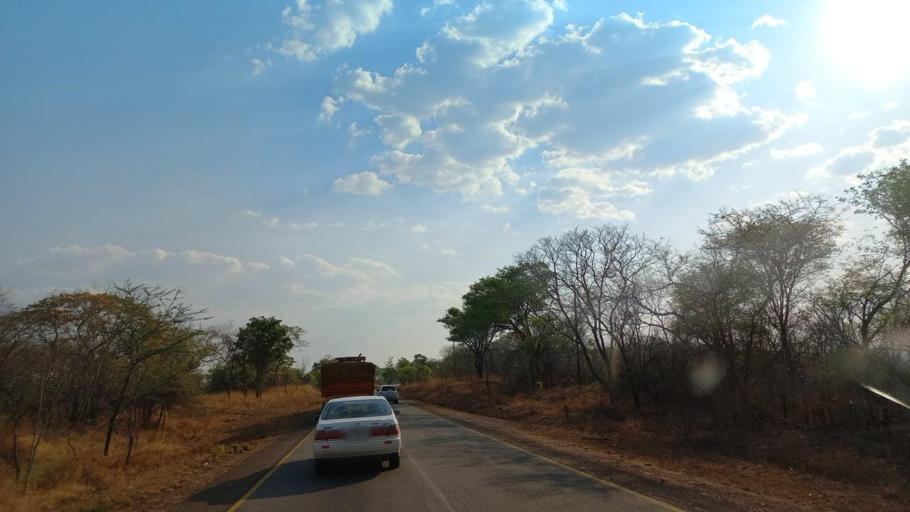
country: ZM
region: Lusaka
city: Luangwa
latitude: -14.9827
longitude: 29.9891
